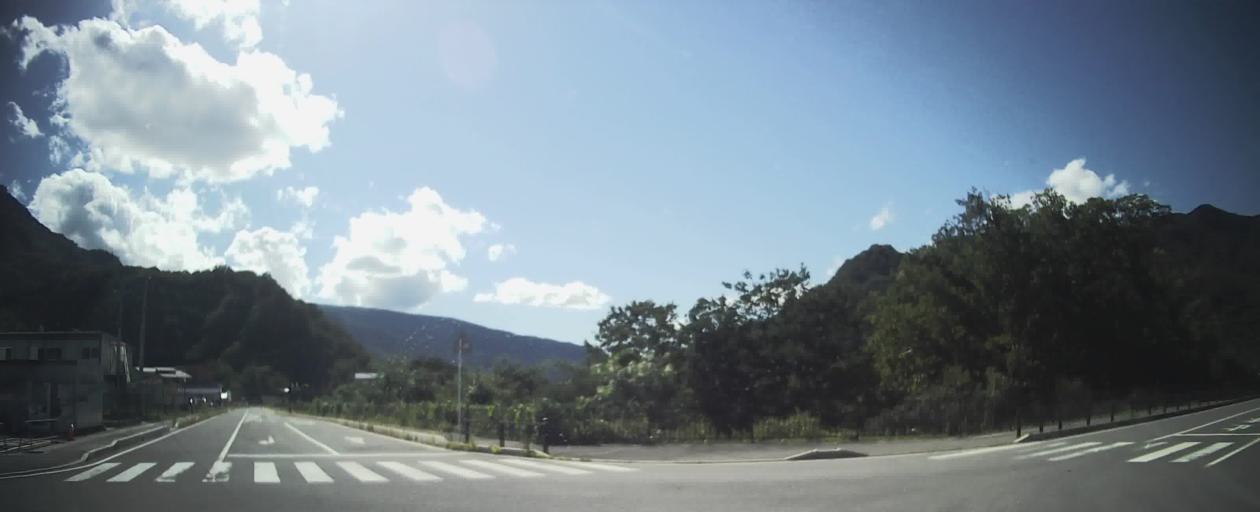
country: JP
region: Gunma
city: Nakanojomachi
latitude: 36.5510
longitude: 138.7079
